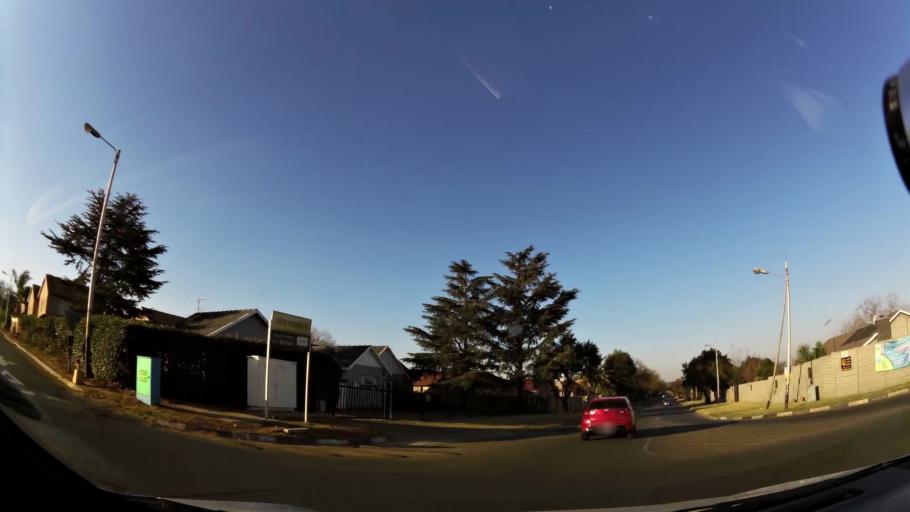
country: ZA
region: Gauteng
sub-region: Ekurhuleni Metropolitan Municipality
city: Germiston
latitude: -26.2743
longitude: 28.1083
